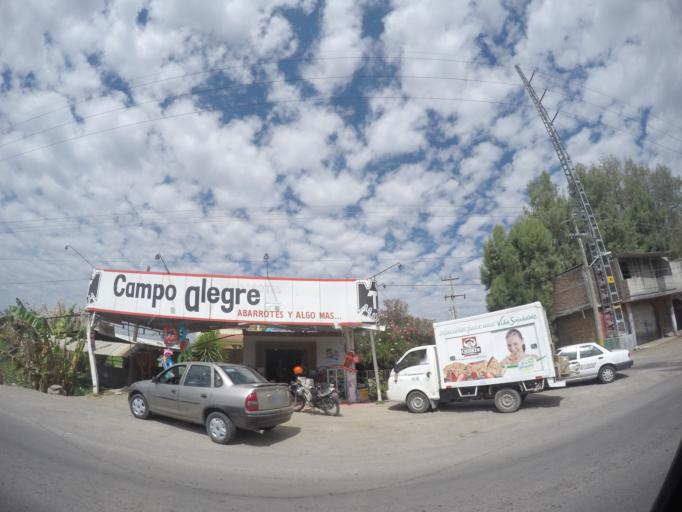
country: MX
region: Guanajuato
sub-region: Leon
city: Santa Ana
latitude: 21.0523
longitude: -101.6888
